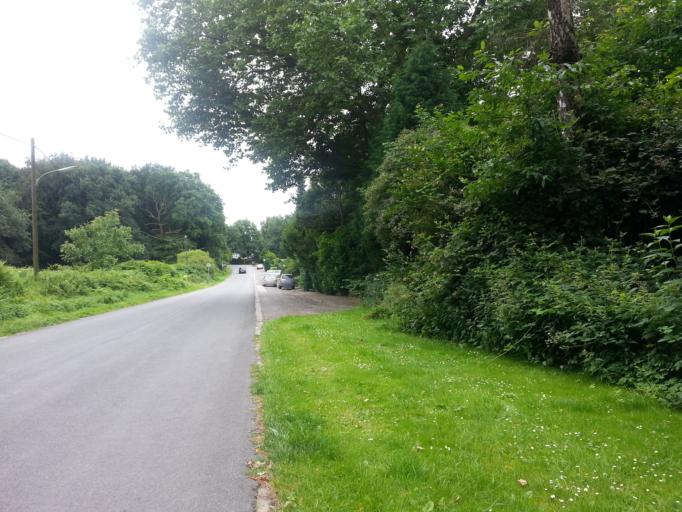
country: DE
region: North Rhine-Westphalia
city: Oer-Erkenschwick
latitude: 51.6594
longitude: 7.2331
